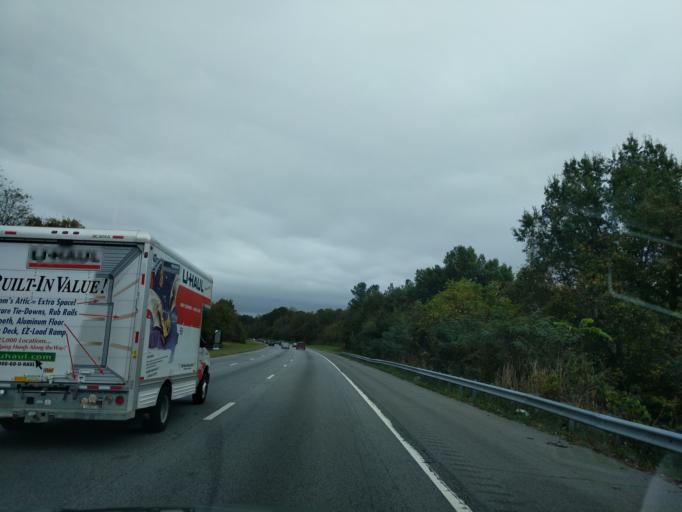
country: US
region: North Carolina
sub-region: Randolph County
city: Trinity
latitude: 35.8687
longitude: -80.0183
